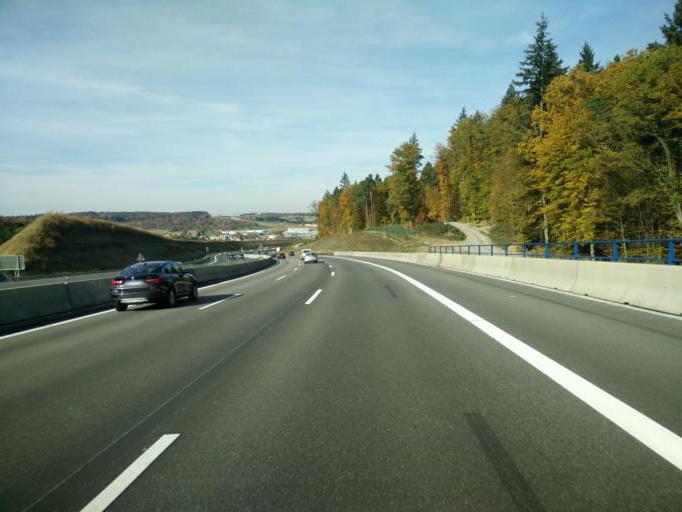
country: DE
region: Baden-Wuerttemberg
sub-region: Karlsruhe Region
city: Konigsbach-Stein
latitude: 48.9286
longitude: 8.5854
